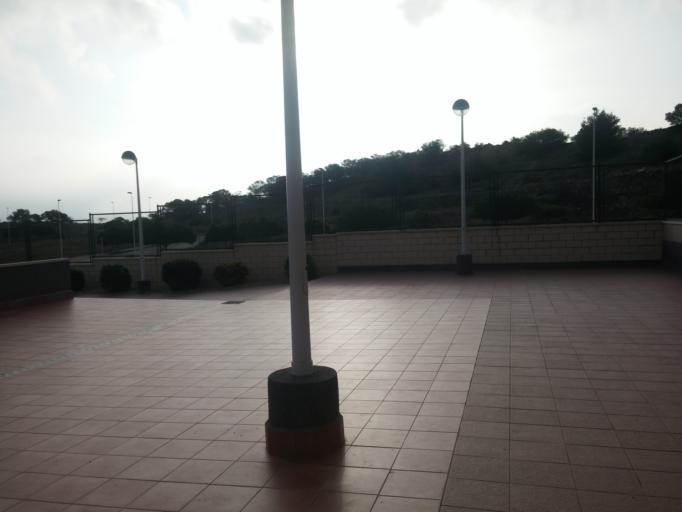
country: ES
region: Valencia
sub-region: Provincia de Alicante
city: Villajoyosa
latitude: 38.5010
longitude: -0.2444
